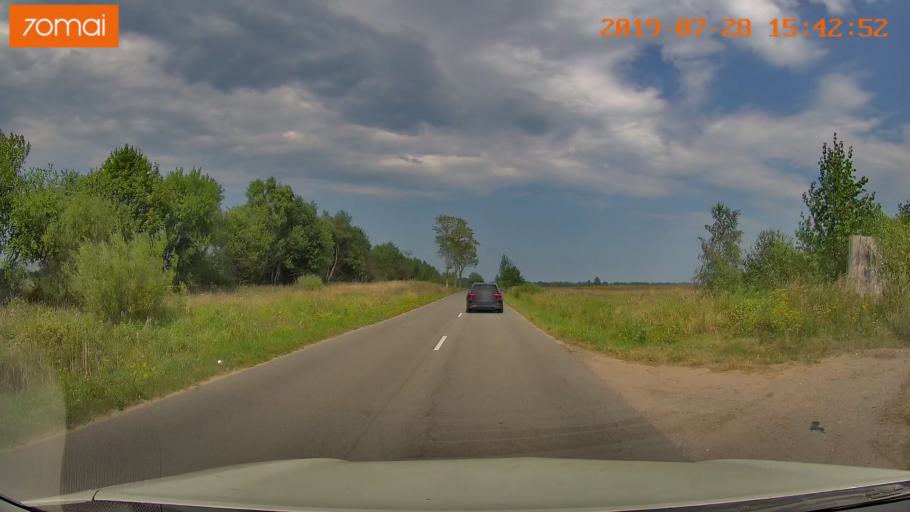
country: RU
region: Kaliningrad
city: Donskoye
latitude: 54.9336
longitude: 20.0170
